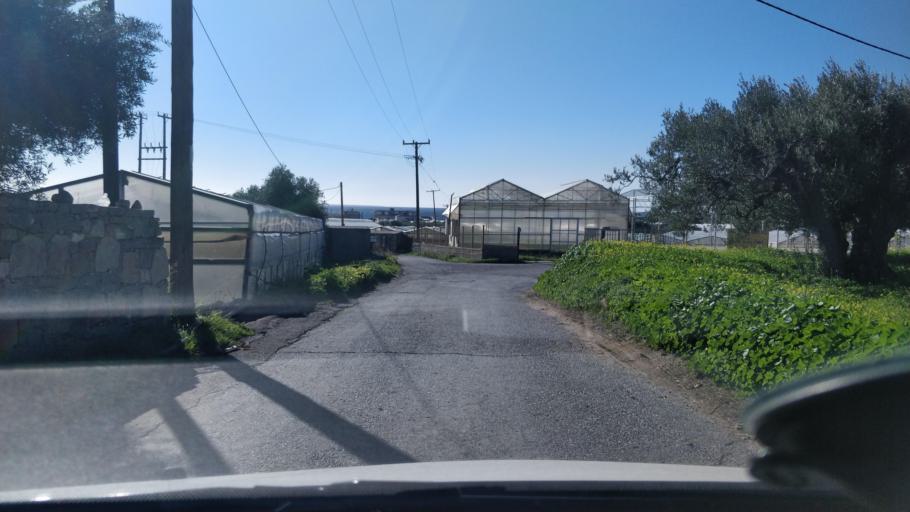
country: GR
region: Crete
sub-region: Nomos Lasithiou
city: Gra Liyia
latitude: 35.0192
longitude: 25.6784
